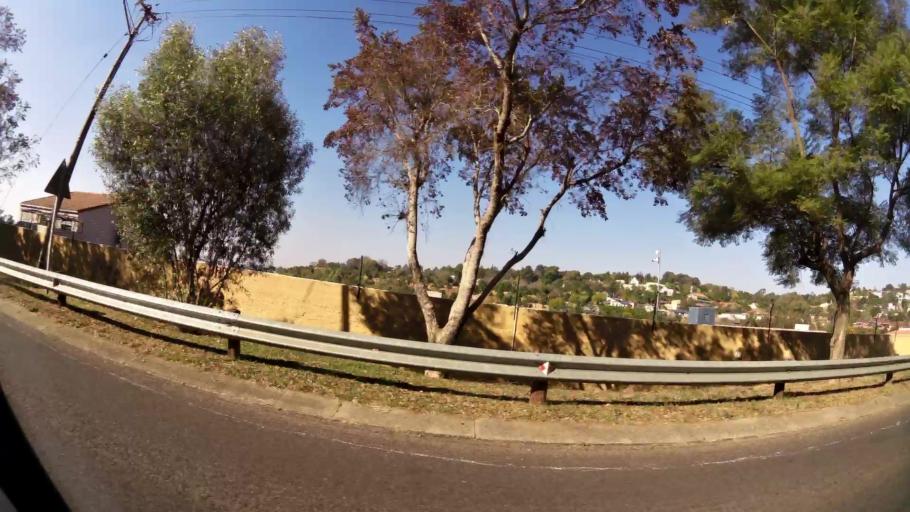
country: ZA
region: Gauteng
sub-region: City of Tshwane Metropolitan Municipality
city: Pretoria
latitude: -25.7892
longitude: 28.2509
